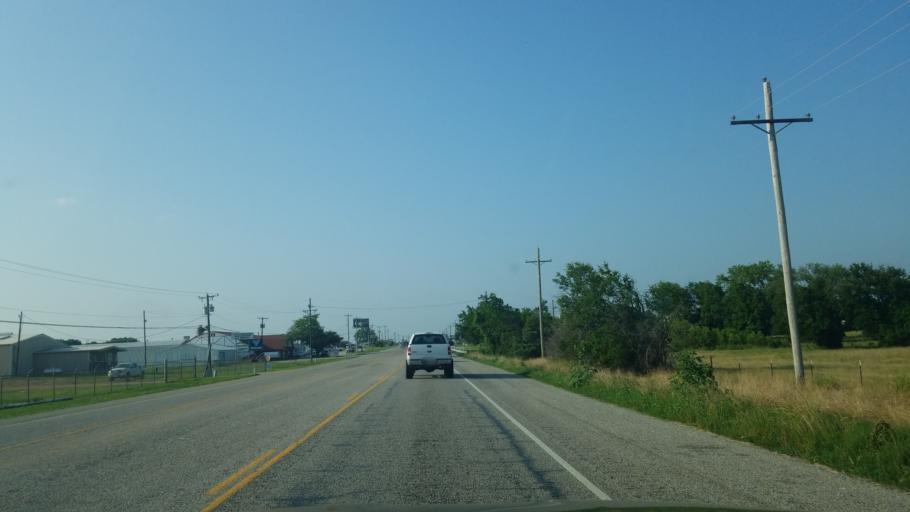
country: US
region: Texas
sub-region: Denton County
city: Pilot Point
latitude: 33.4022
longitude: -96.9438
